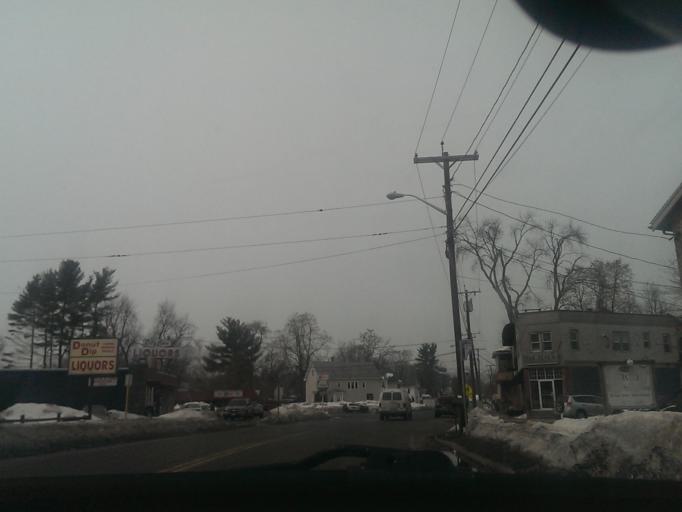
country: US
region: Massachusetts
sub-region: Hampden County
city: East Longmeadow
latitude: 42.0805
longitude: -72.5379
